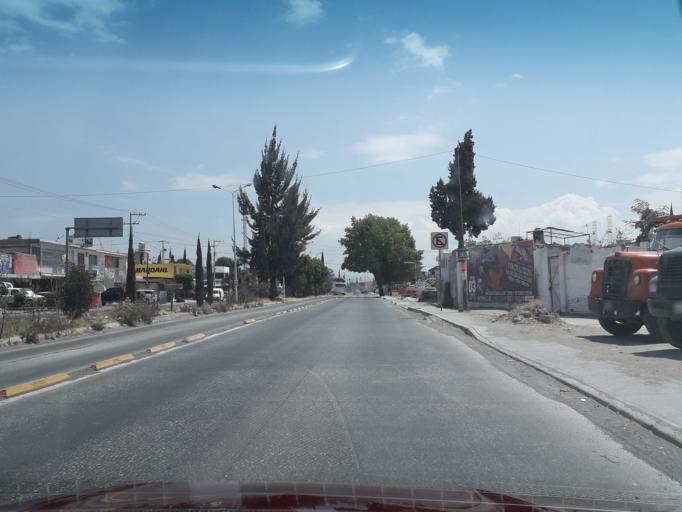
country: MX
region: Puebla
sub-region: Puebla
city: El Capulo (La Quebradora)
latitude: 18.9737
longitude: -98.2602
